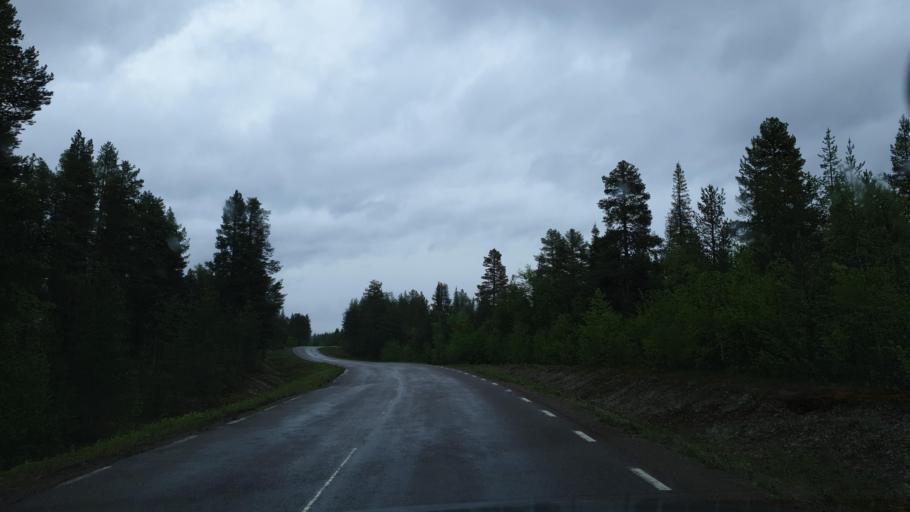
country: SE
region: Norrbotten
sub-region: Kiruna Kommun
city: Kiruna
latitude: 67.8831
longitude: 21.0041
